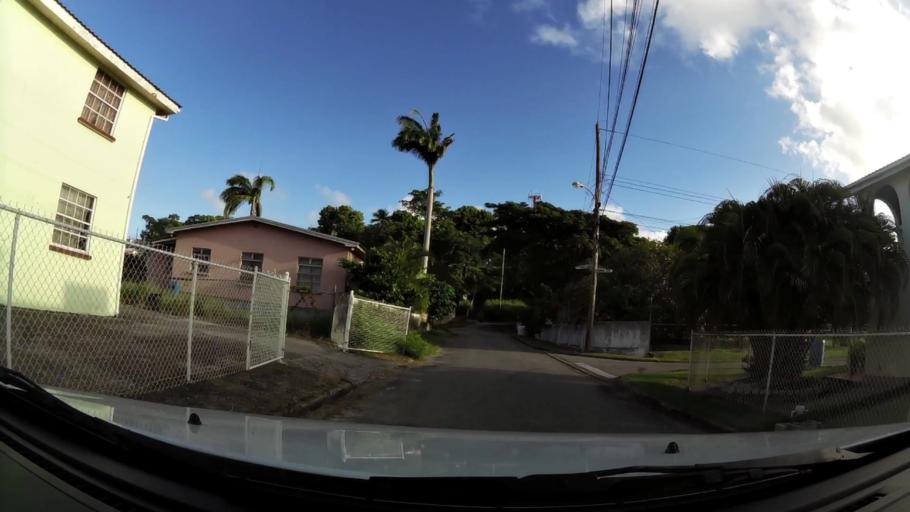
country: BB
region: Christ Church
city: Oistins
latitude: 13.0690
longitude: -59.5534
